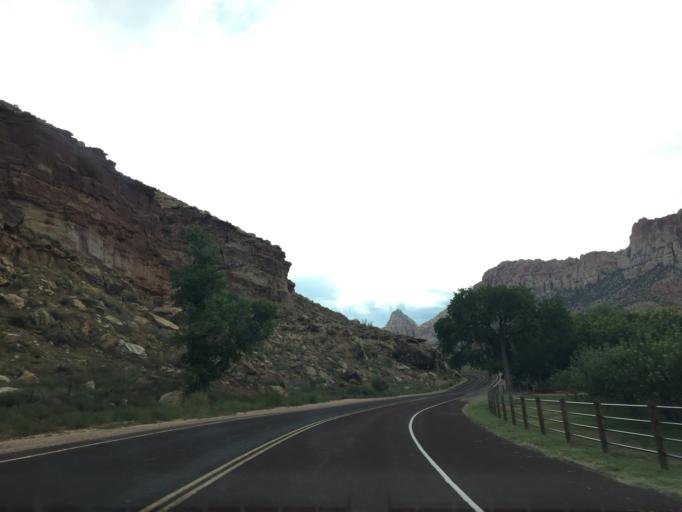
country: US
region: Utah
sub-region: Washington County
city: Hildale
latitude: 37.1629
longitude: -113.0173
